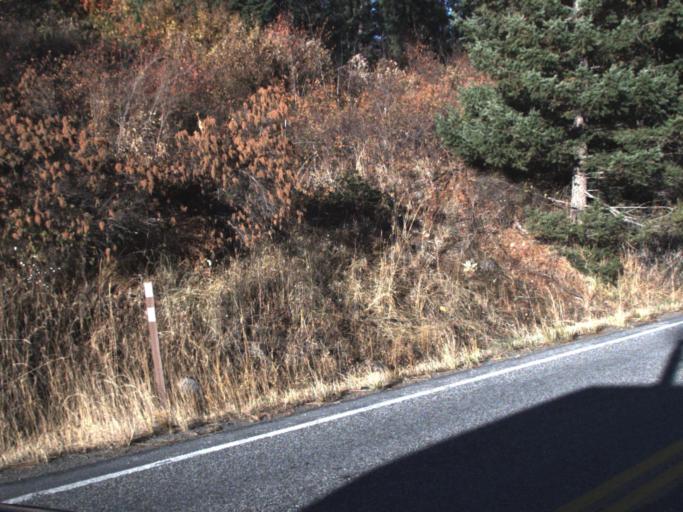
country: US
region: Washington
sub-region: Okanogan County
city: Coulee Dam
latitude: 48.0809
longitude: -118.6888
